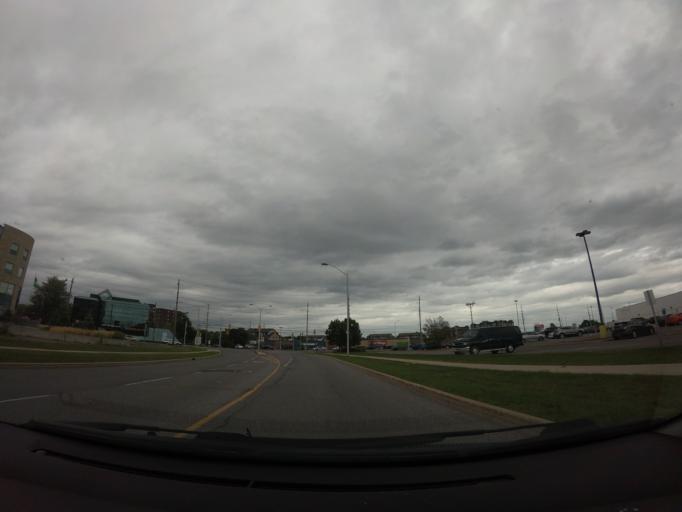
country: CA
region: Ontario
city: Ottawa
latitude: 45.4227
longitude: -75.6307
